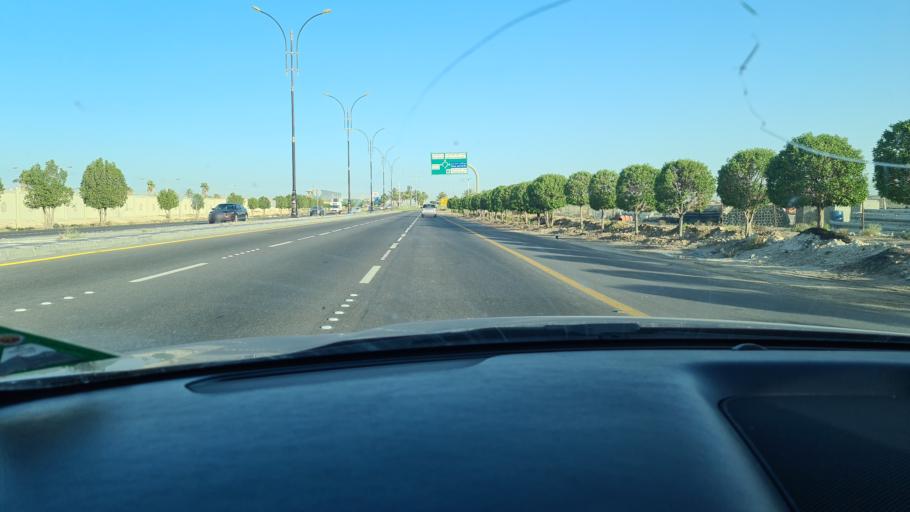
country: SA
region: Eastern Province
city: Al Jubayl
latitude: 26.9300
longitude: 49.7095
